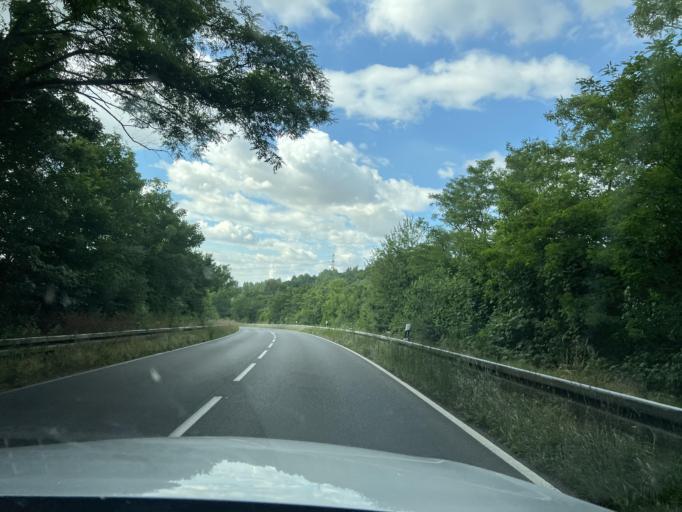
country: DE
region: North Rhine-Westphalia
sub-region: Regierungsbezirk Koln
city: Bergheim
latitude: 50.9589
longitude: 6.6903
